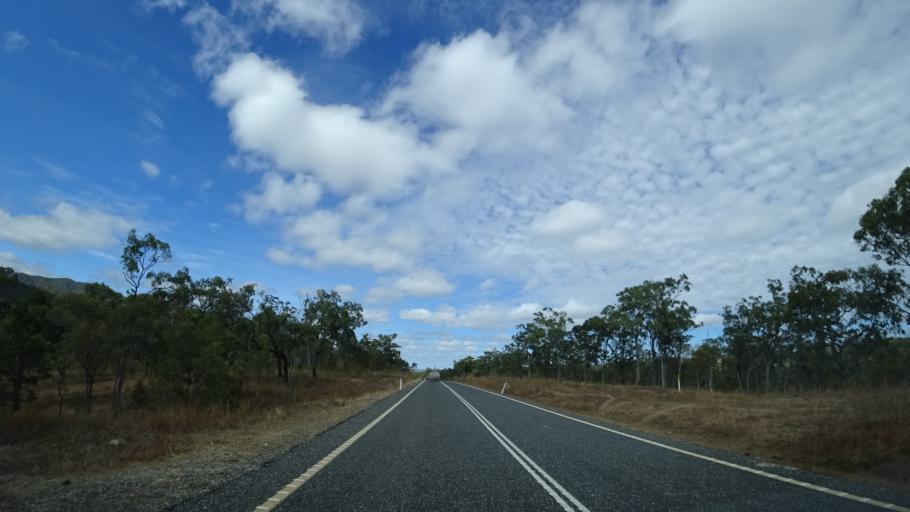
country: AU
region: Queensland
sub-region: Cairns
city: Port Douglas
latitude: -16.3165
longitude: 144.7184
